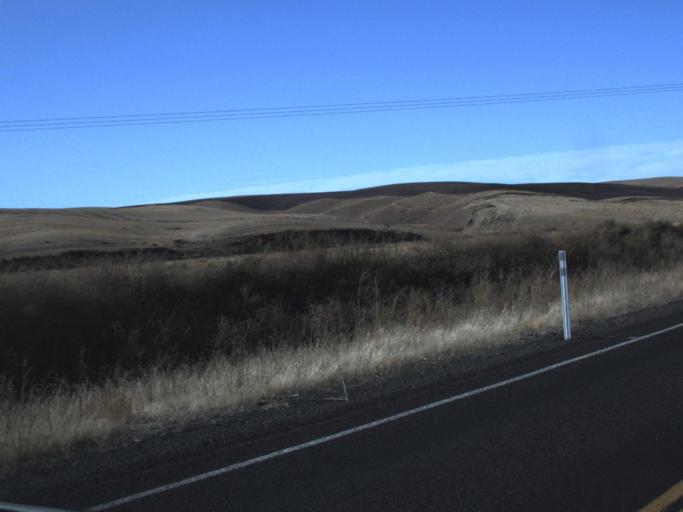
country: US
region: Washington
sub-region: Walla Walla County
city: Walla Walla
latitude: 46.1655
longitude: -118.3809
